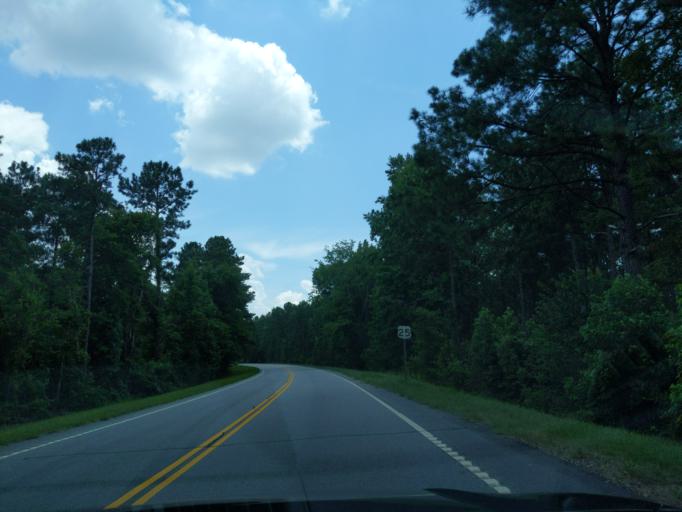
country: US
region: South Carolina
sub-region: Greenwood County
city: Ninety Six
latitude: 34.0001
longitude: -82.0489
